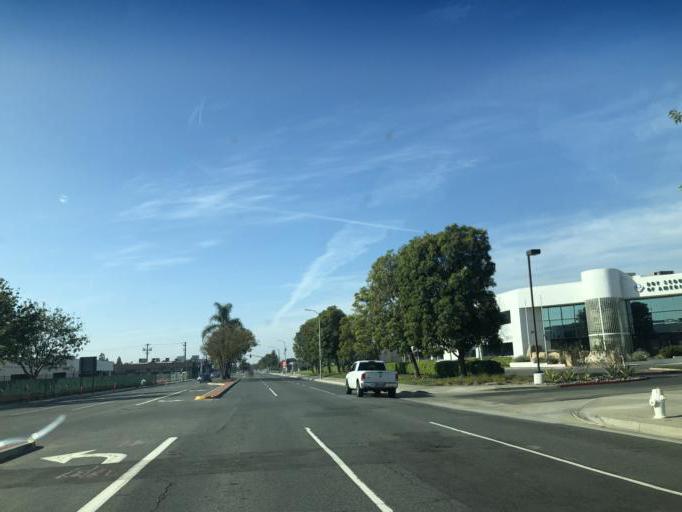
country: US
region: California
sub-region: Orange County
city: Santa Ana
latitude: 33.7087
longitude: -117.8573
